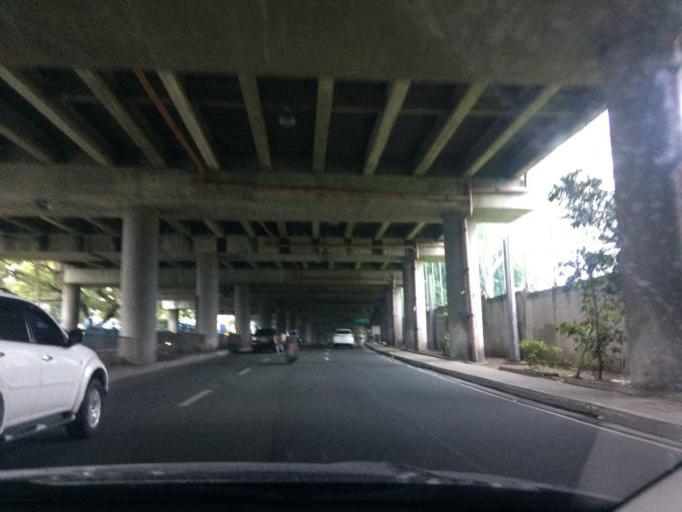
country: PH
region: Metro Manila
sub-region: Makati City
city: Makati City
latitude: 14.5217
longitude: 121.0237
